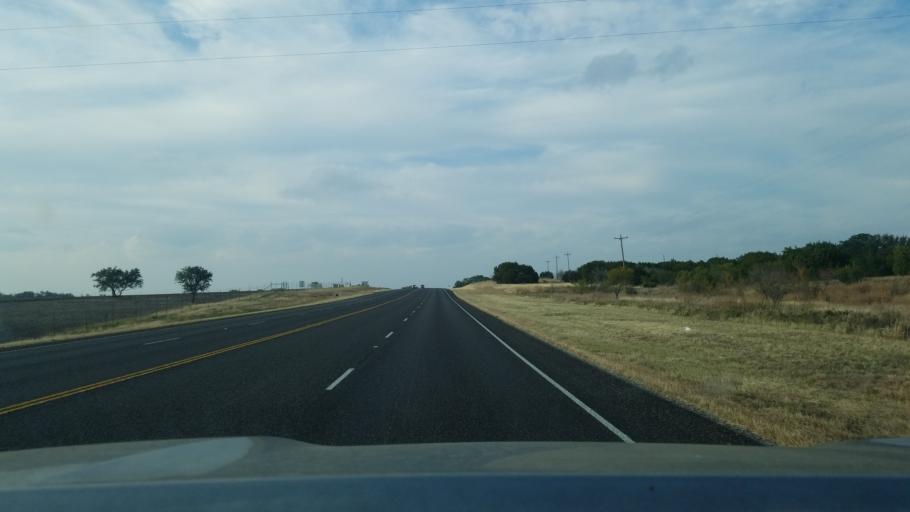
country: US
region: Texas
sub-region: Mills County
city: Goldthwaite
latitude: 31.2884
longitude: -98.4622
